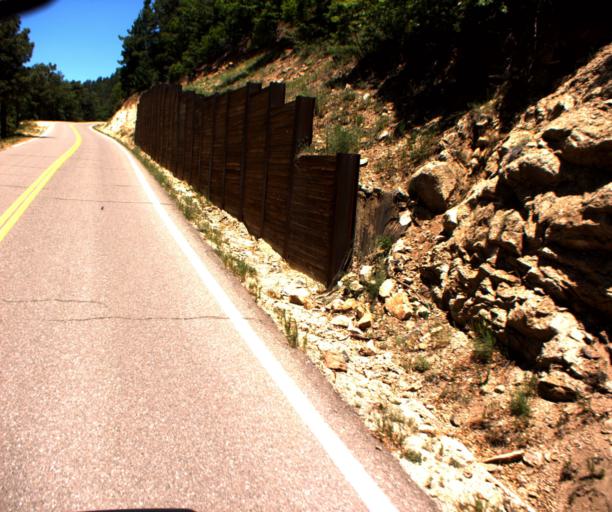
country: US
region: Arizona
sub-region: Graham County
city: Swift Trail Junction
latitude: 32.6237
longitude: -109.8324
